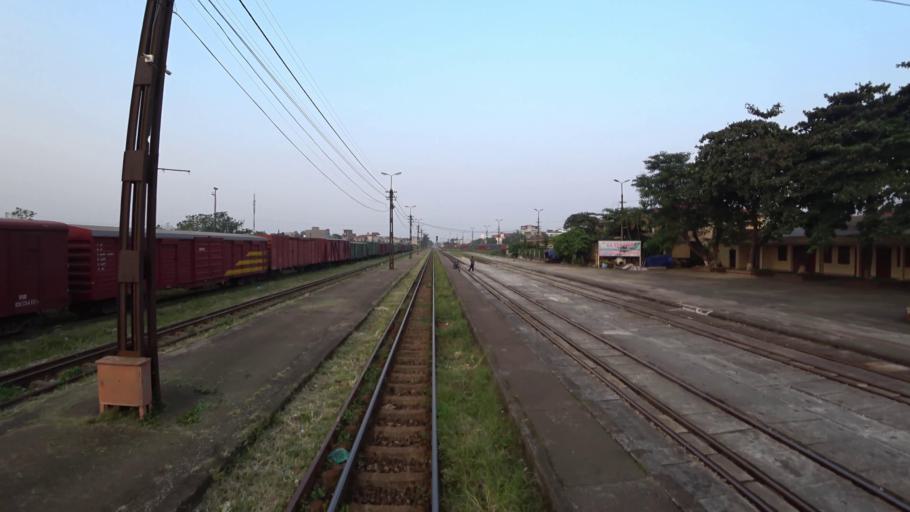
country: VN
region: Ha Noi
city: Dong Anh
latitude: 21.0982
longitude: 105.9087
